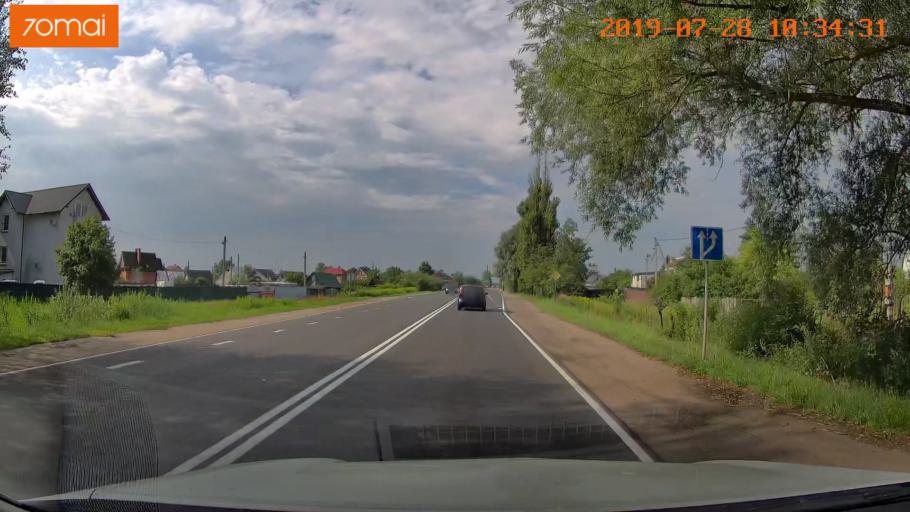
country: RU
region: Kaliningrad
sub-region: Gorod Kaliningrad
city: Kaliningrad
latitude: 54.7528
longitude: 20.4386
